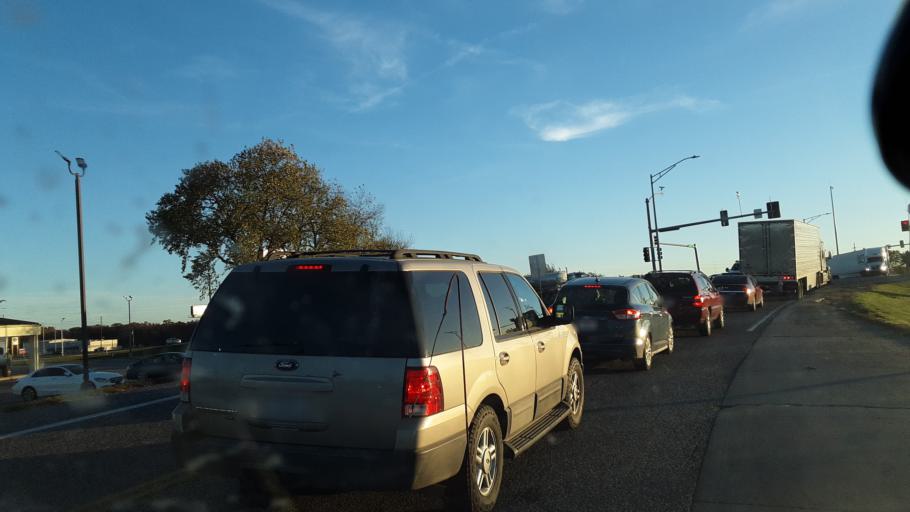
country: US
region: Missouri
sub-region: Warren County
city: Wright City
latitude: 38.8183
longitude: -90.9522
